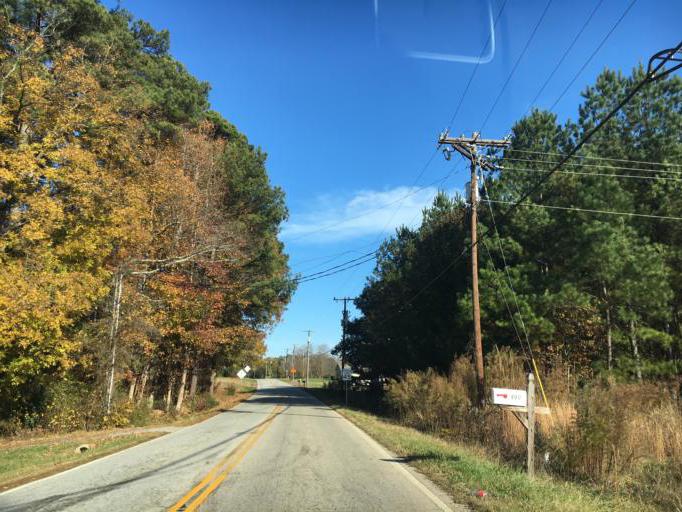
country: US
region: South Carolina
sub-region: Spartanburg County
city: Fairforest
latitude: 34.9975
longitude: -82.0548
